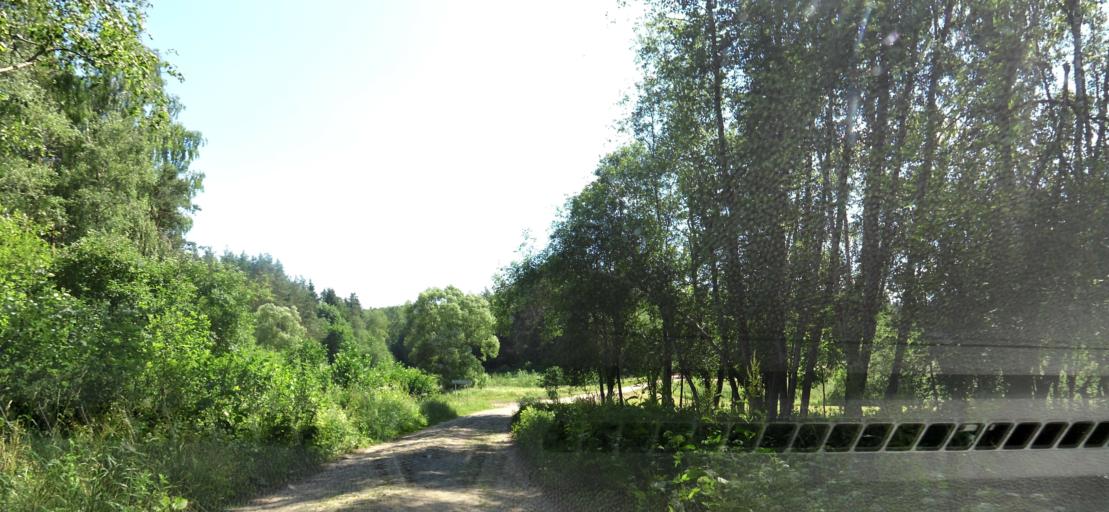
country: LT
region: Vilnius County
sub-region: Vilnius
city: Fabijoniskes
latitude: 54.8309
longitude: 25.3242
